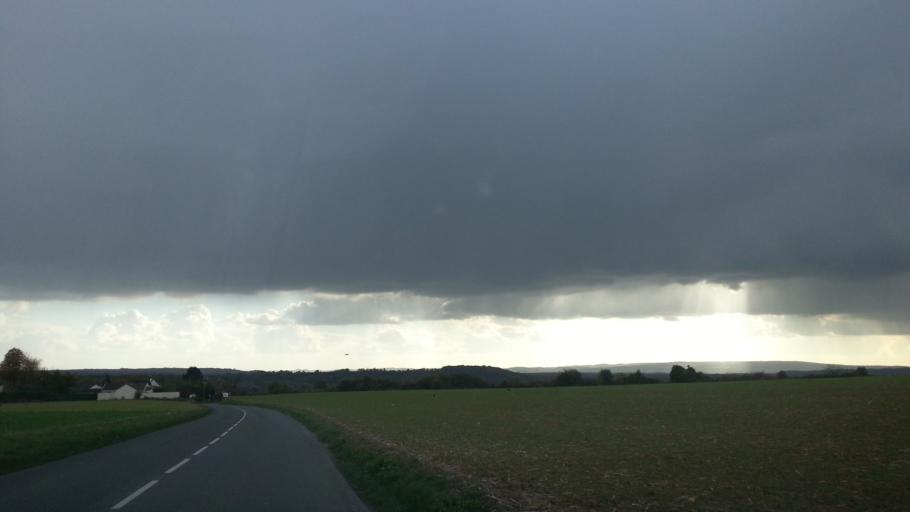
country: FR
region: Picardie
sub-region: Departement de l'Oise
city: Villers-sous-Saint-Leu
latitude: 49.2261
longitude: 2.4142
